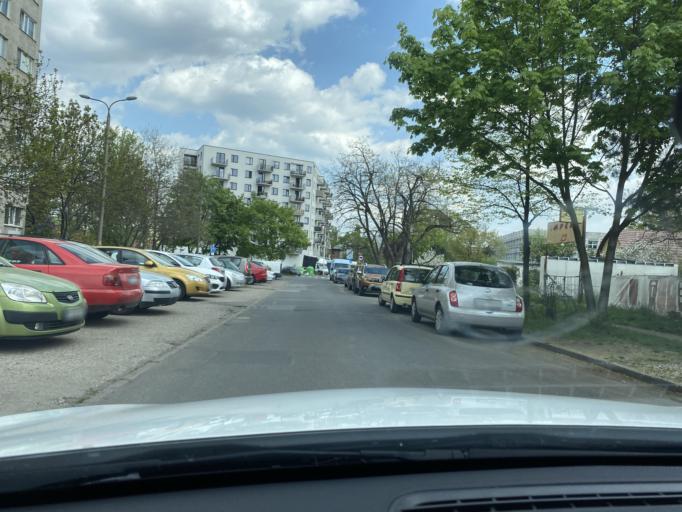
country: PL
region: Lower Silesian Voivodeship
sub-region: Powiat wroclawski
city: Wroclaw
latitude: 51.1366
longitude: 17.0254
